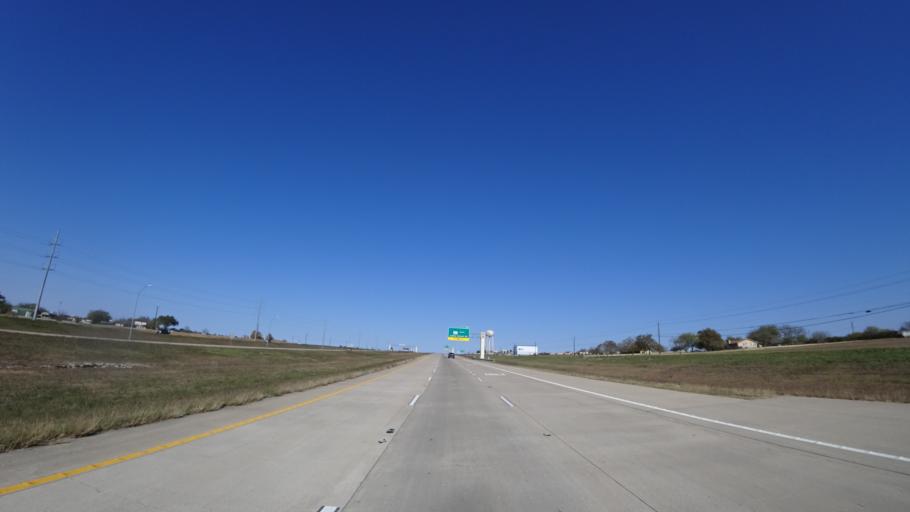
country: US
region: Texas
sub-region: Travis County
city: Pflugerville
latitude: 30.4860
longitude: -97.5844
